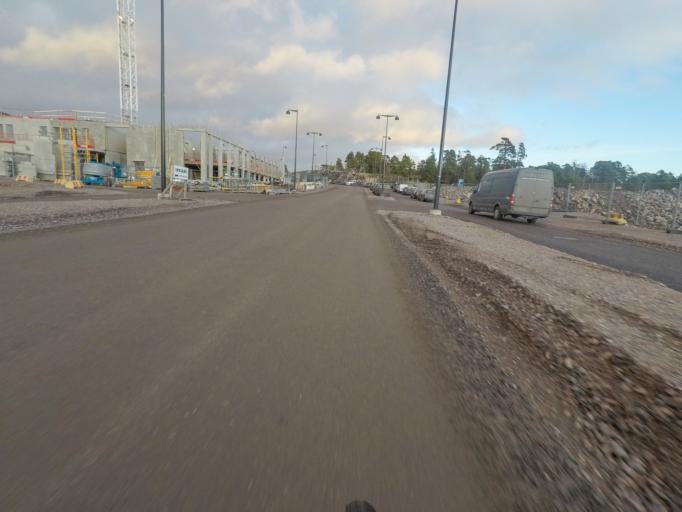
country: FI
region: Uusimaa
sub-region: Helsinki
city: Helsinki
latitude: 60.1659
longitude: 25.0188
